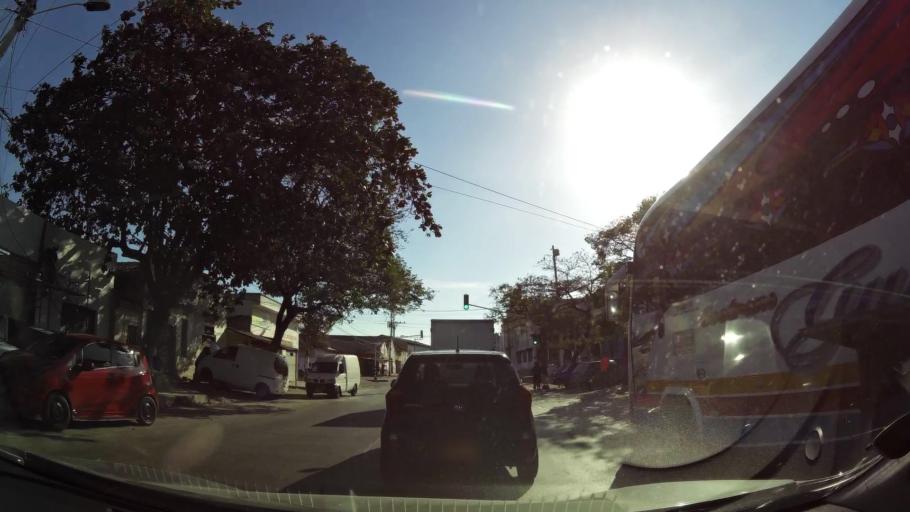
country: CO
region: Atlantico
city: Barranquilla
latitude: 10.9663
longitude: -74.7896
